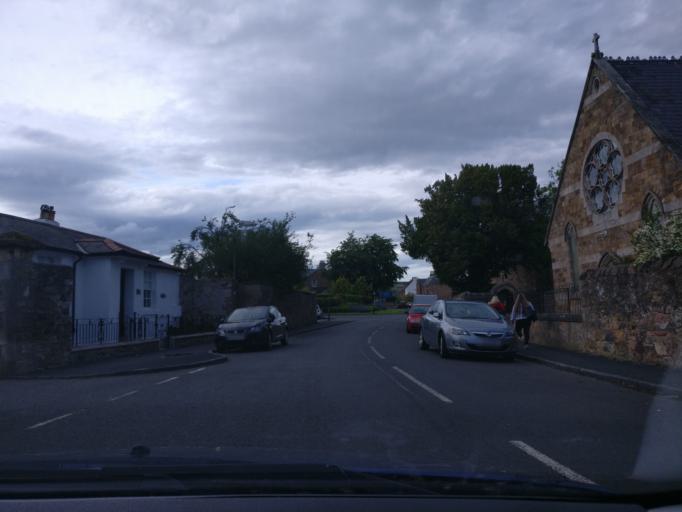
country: GB
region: Scotland
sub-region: East Lothian
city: Haddington
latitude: 55.9522
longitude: -2.7741
